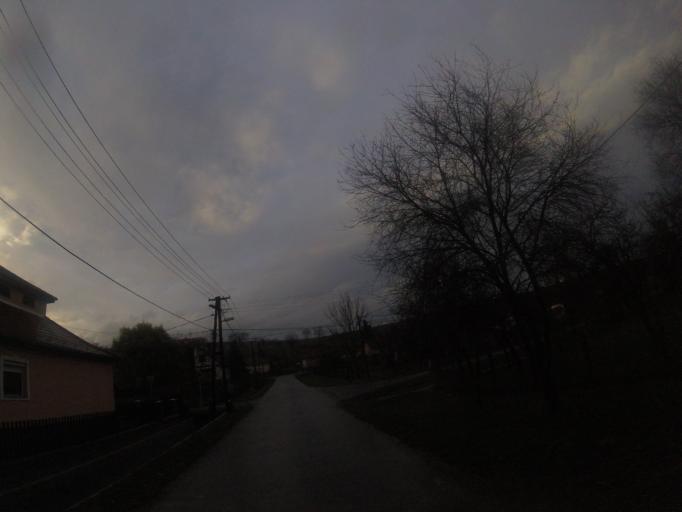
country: HU
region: Nograd
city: Rimoc
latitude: 48.0121
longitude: 19.5029
